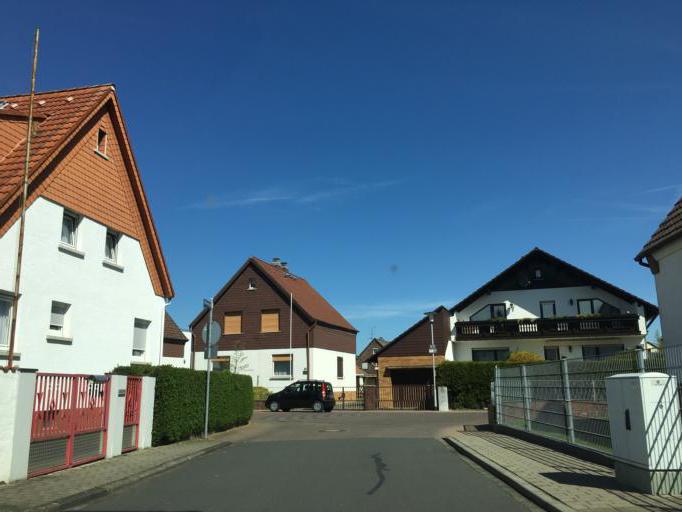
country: DE
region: Hesse
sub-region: Regierungsbezirk Darmstadt
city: Gross-Zimmern
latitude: 49.8713
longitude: 8.8241
